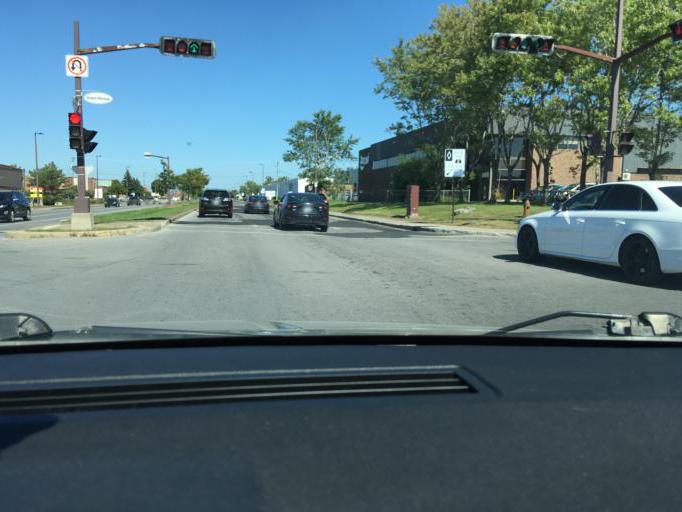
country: CA
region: Quebec
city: Dorval
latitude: 45.5009
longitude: -73.7466
